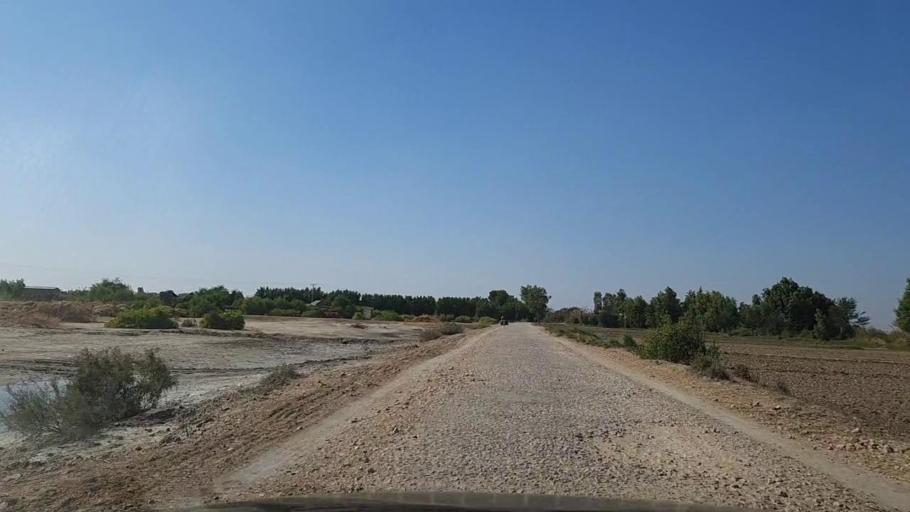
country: PK
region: Sindh
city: Mirpur Sakro
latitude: 24.6124
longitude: 67.7794
